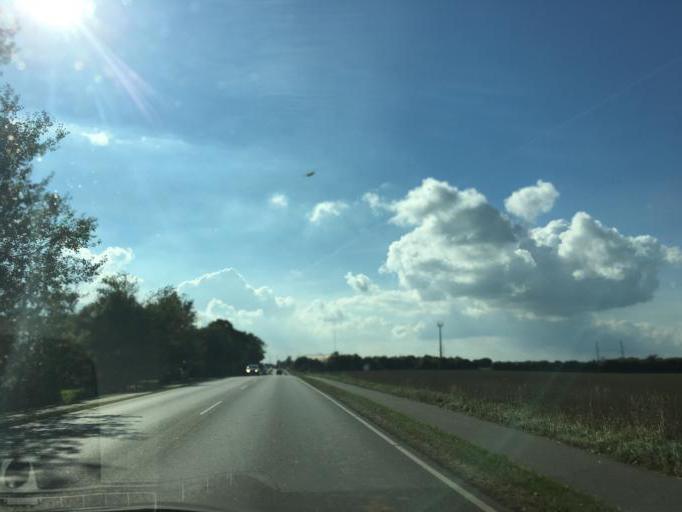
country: DK
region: South Denmark
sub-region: Fredericia Kommune
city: Snoghoj
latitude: 55.5650
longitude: 9.6828
